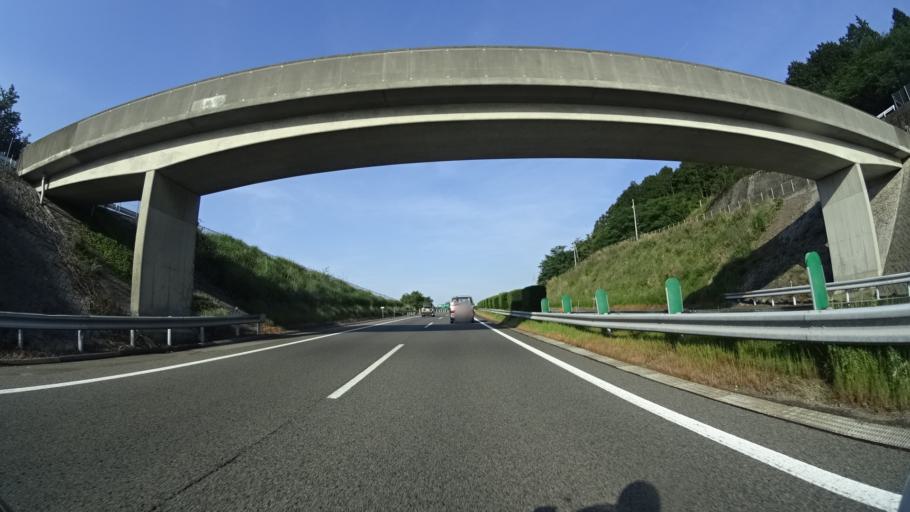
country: JP
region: Ehime
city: Niihama
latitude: 33.9516
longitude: 133.4390
